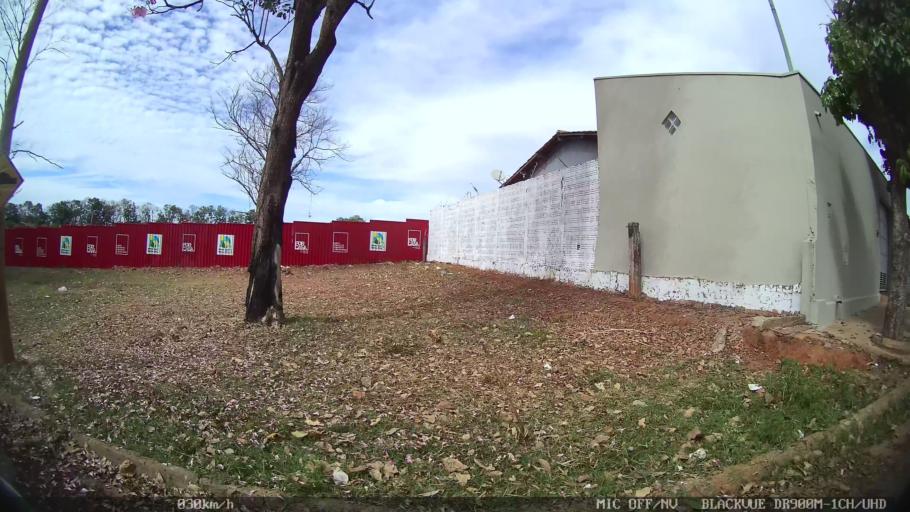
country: BR
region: Sao Paulo
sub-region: Catanduva
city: Catanduva
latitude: -21.1563
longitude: -48.9733
